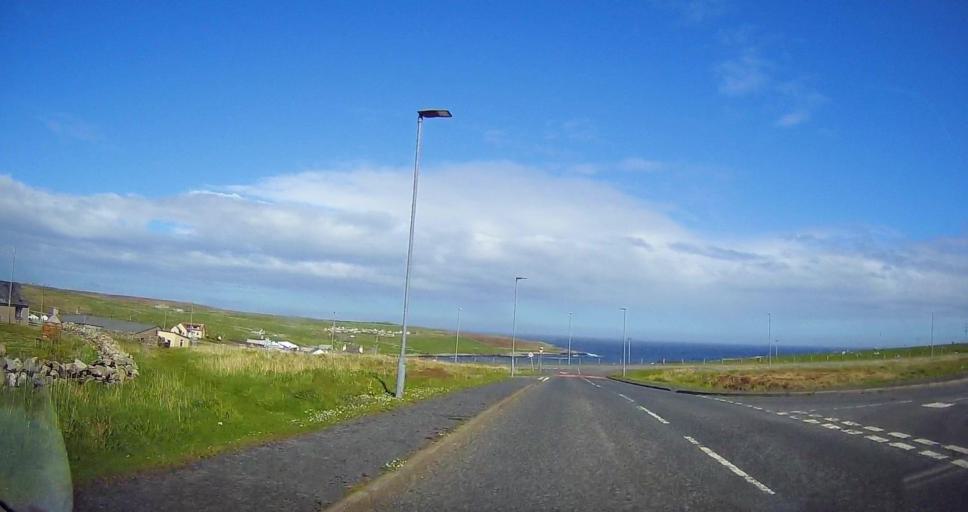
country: GB
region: Scotland
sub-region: Shetland Islands
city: Sandwick
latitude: 59.9195
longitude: -1.3015
